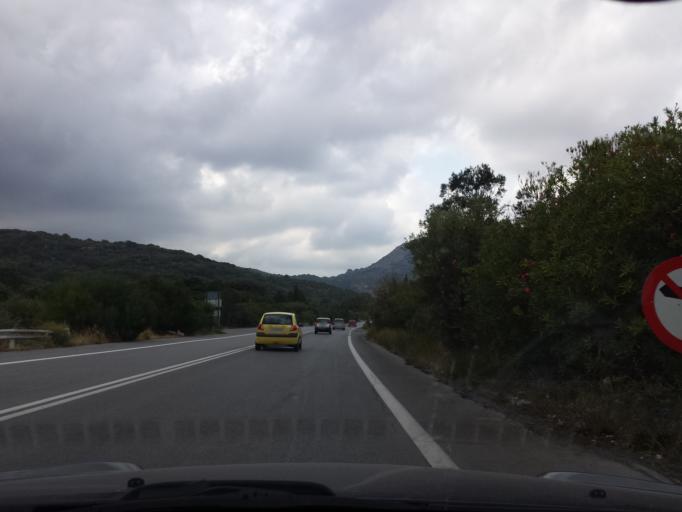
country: GR
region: Crete
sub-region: Nomos Lasithiou
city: Neapoli
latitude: 35.2618
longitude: 25.5942
